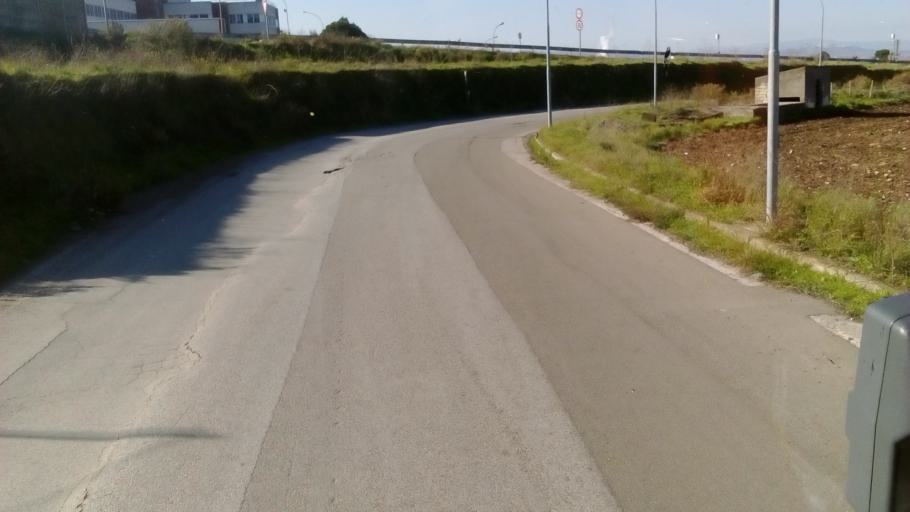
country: IT
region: Basilicate
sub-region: Provincia di Potenza
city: Melfi
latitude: 41.0775
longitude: 15.6738
